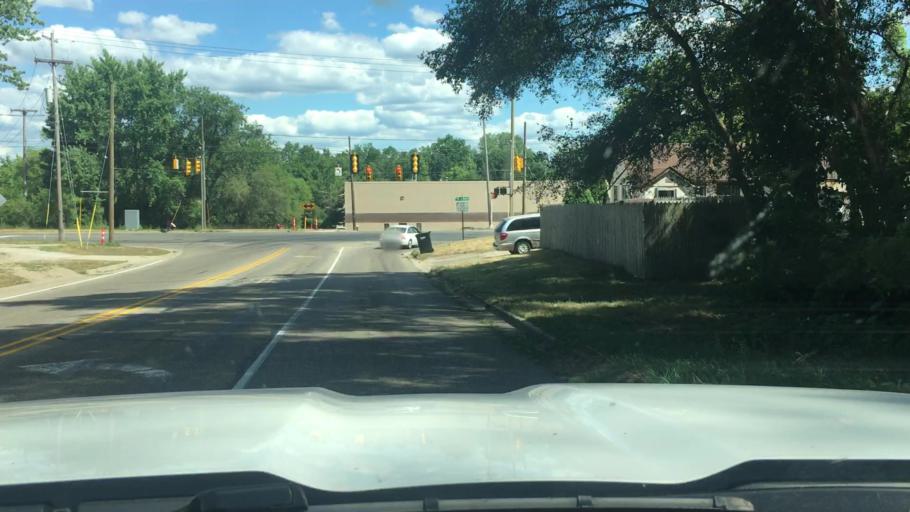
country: US
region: Michigan
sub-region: Kent County
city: Comstock Park
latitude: 43.0524
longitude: -85.6527
